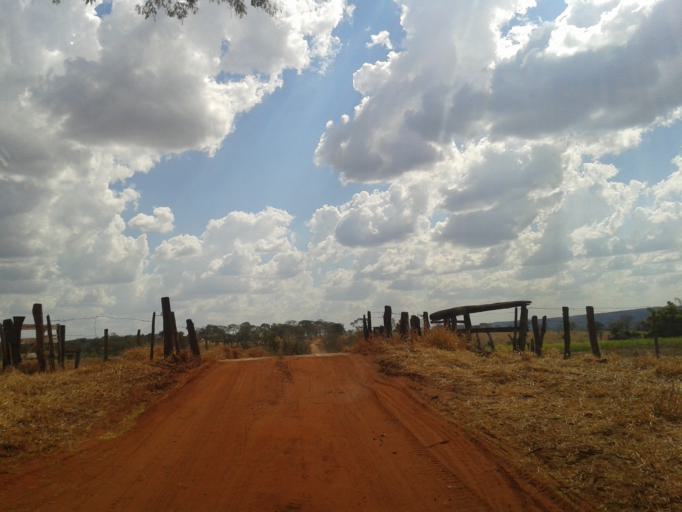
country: BR
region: Minas Gerais
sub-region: Santa Vitoria
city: Santa Vitoria
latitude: -19.2024
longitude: -49.8995
